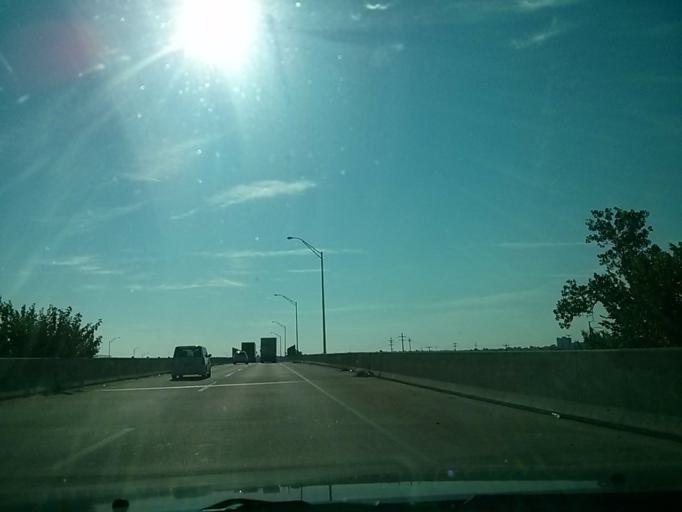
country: US
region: Oklahoma
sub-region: Tulsa County
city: Tulsa
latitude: 36.1601
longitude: -95.9842
